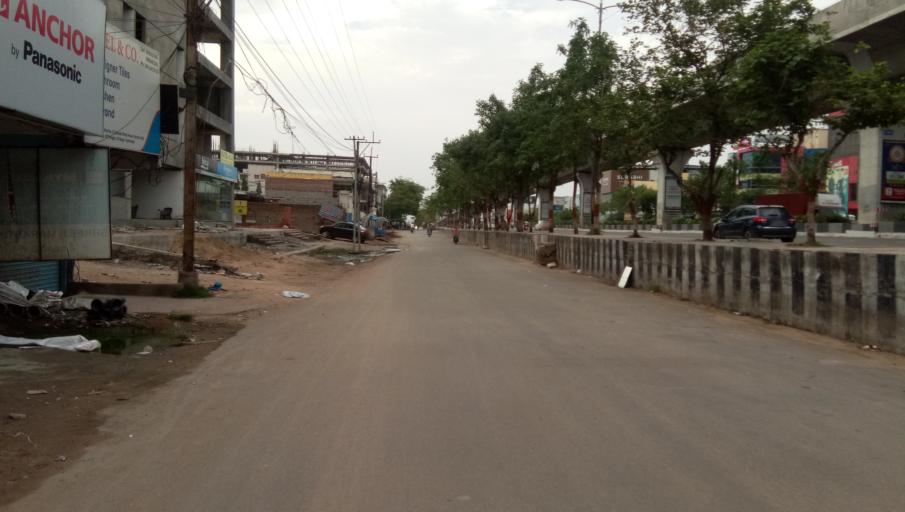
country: IN
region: Telangana
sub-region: Rangareddi
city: Lal Bahadur Nagar
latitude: 17.3568
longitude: 78.5449
